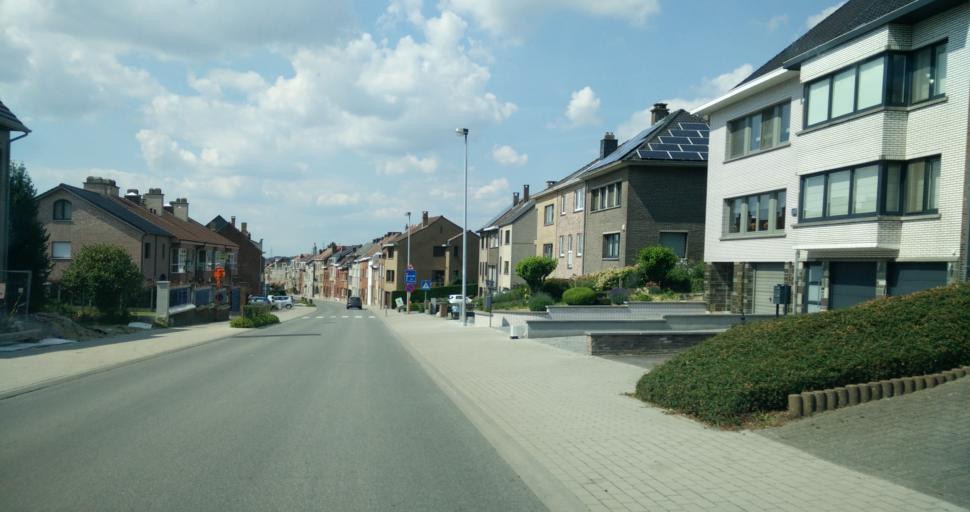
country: BE
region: Flanders
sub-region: Provincie Vlaams-Brabant
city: Halle
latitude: 50.7238
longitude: 4.2480
